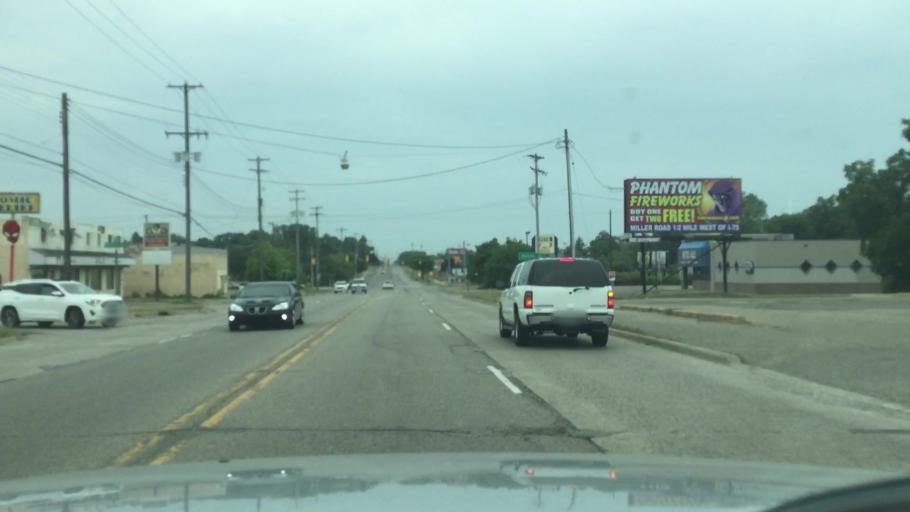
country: US
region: Michigan
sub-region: Genesee County
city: Flint
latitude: 42.9722
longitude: -83.6928
